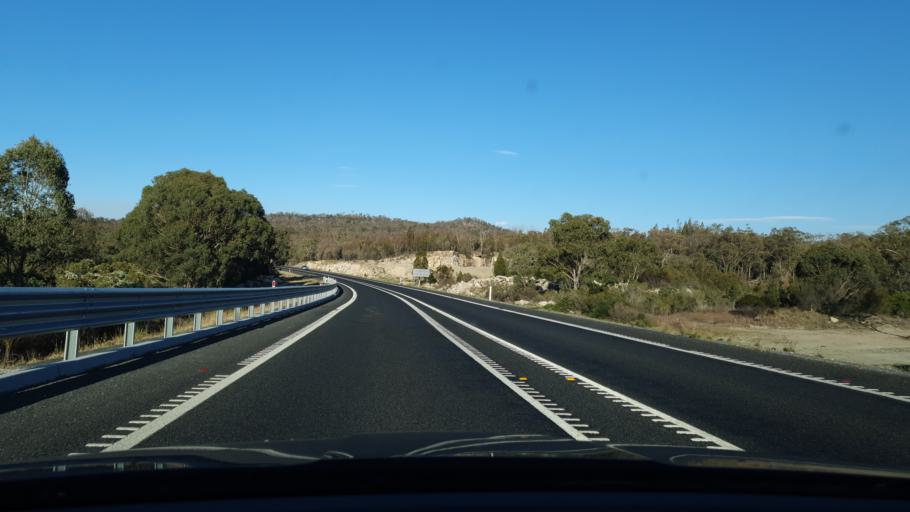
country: AU
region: Queensland
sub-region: Southern Downs
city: Stanthorpe
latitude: -28.6842
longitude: 151.9159
